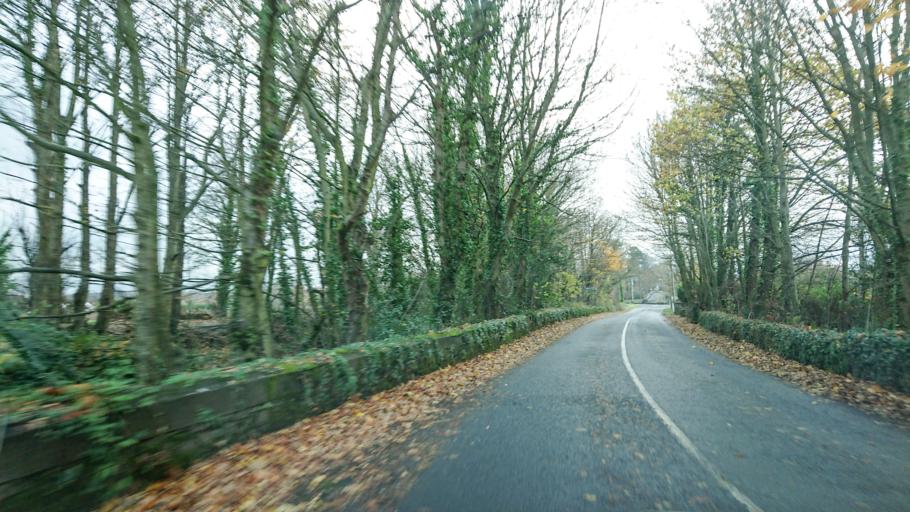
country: IE
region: Munster
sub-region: South Tipperary
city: Cluain Meala
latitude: 52.3543
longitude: -7.6498
